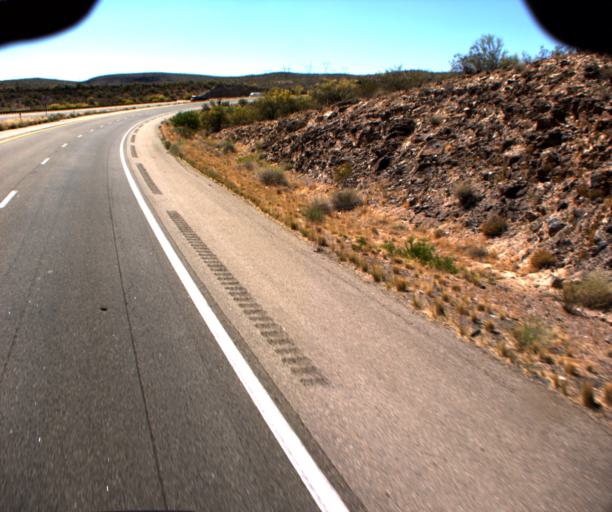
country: US
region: Arizona
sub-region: Yavapai County
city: Bagdad
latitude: 34.5458
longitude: -113.4463
